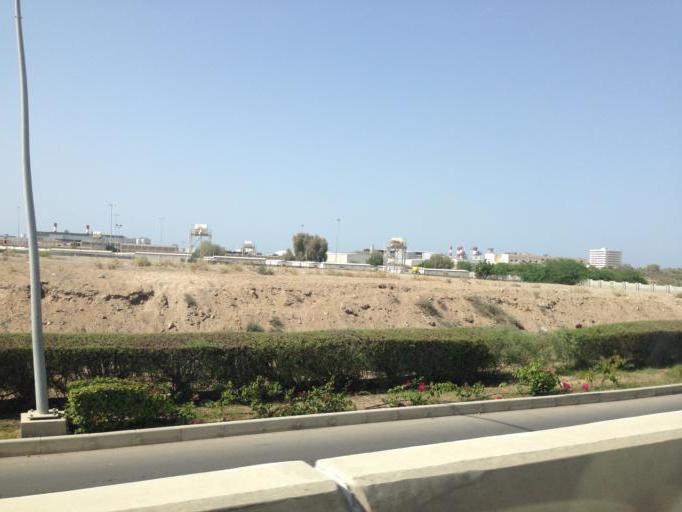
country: OM
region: Muhafazat Masqat
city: Bawshar
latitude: 23.5960
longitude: 58.4120
